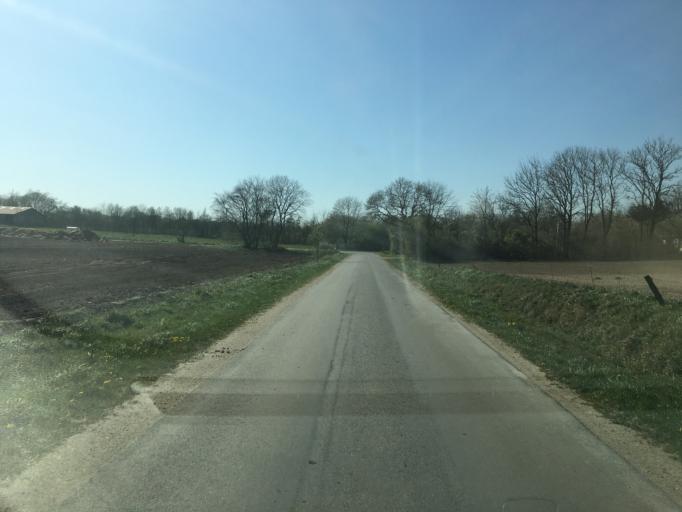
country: DK
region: South Denmark
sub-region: Aabenraa Kommune
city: Rodekro
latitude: 55.0969
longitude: 9.2404
